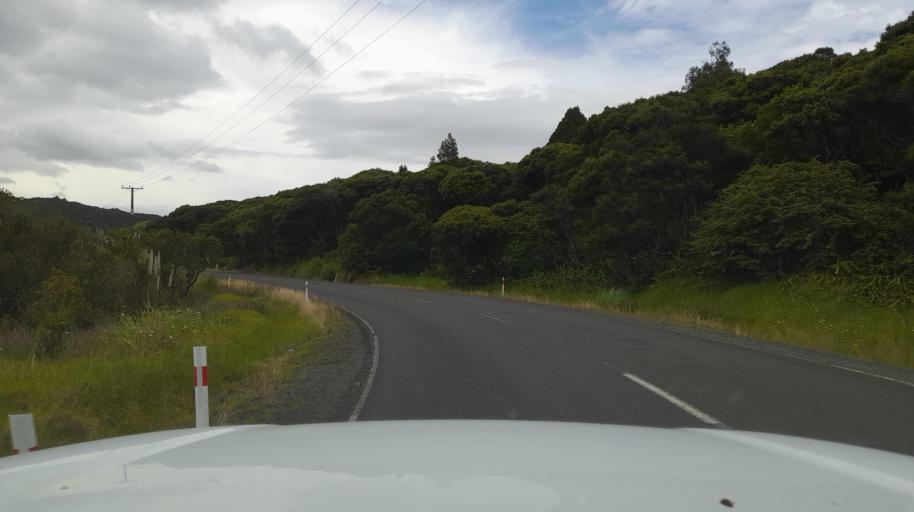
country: NZ
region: Northland
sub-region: Far North District
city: Kaitaia
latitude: -35.3952
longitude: 173.3803
